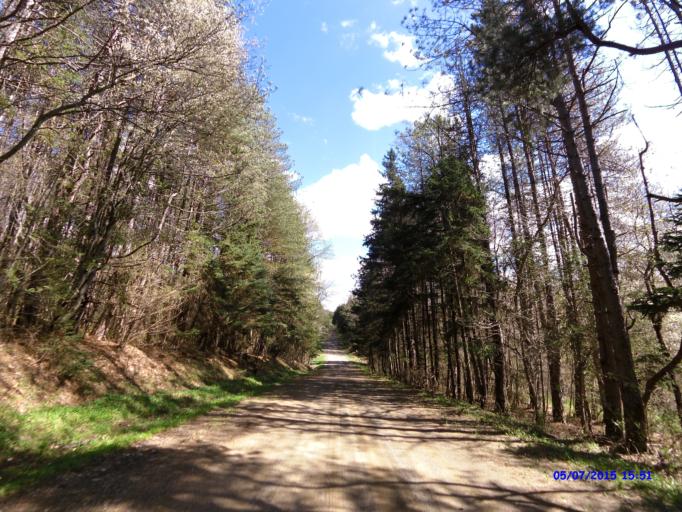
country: US
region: New York
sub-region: Cattaraugus County
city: Franklinville
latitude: 42.3302
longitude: -78.5442
